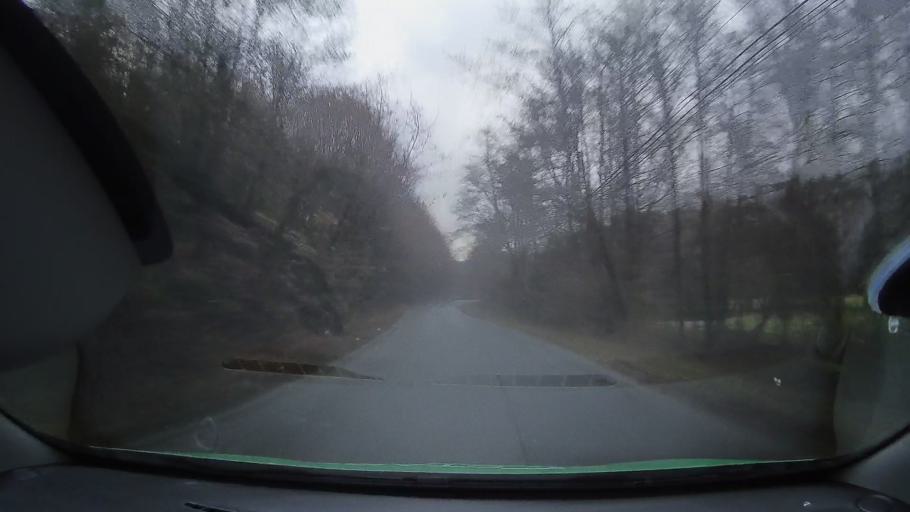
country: RO
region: Hunedoara
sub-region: Comuna Baia de Cris
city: Baia de Cris
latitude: 46.1962
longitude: 22.7173
